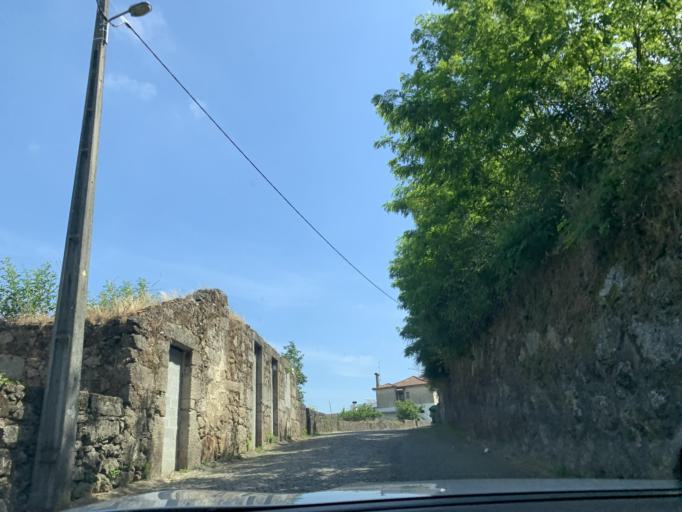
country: PT
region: Viseu
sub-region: Viseu
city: Viseu
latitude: 40.6574
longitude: -7.9323
